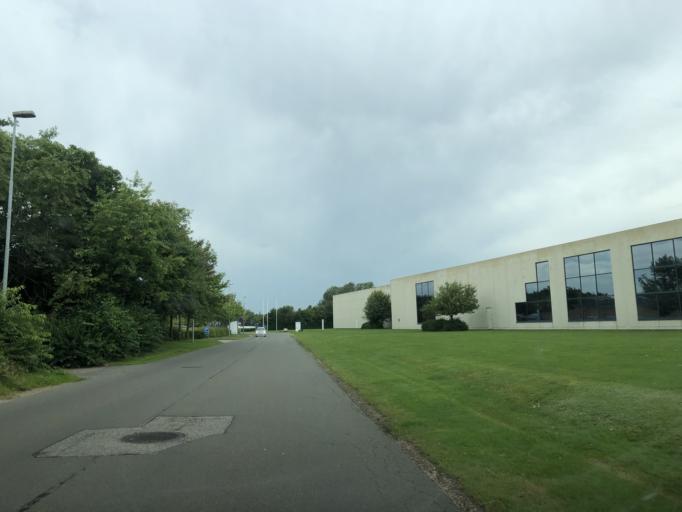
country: DK
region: Central Jutland
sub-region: Holstebro Kommune
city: Holstebro
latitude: 56.3835
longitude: 8.6082
